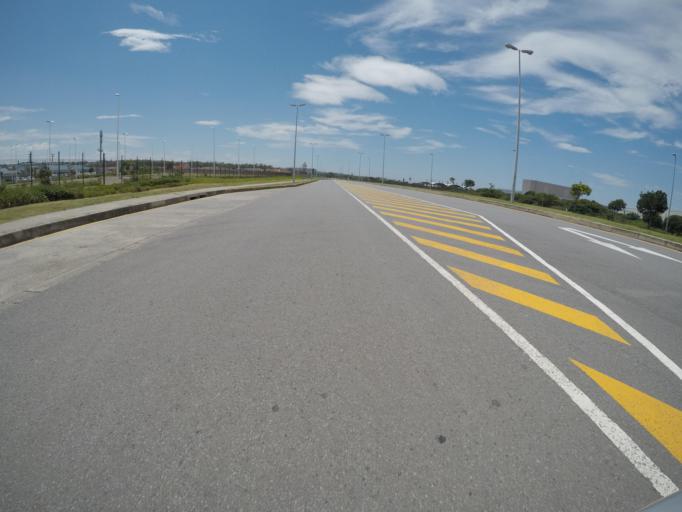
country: ZA
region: Eastern Cape
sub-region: Buffalo City Metropolitan Municipality
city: East London
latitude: -33.0512
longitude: 27.8484
